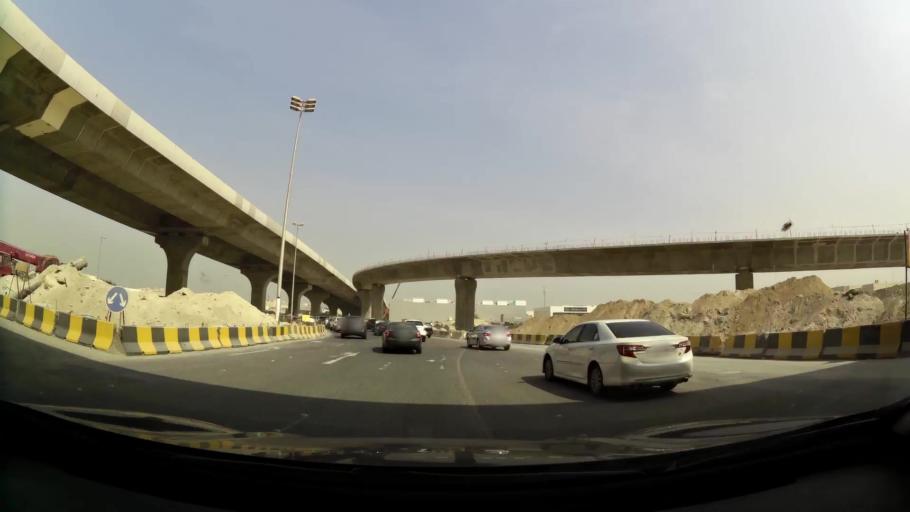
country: KW
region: Al Asimah
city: Ash Shamiyah
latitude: 29.3315
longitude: 47.9311
